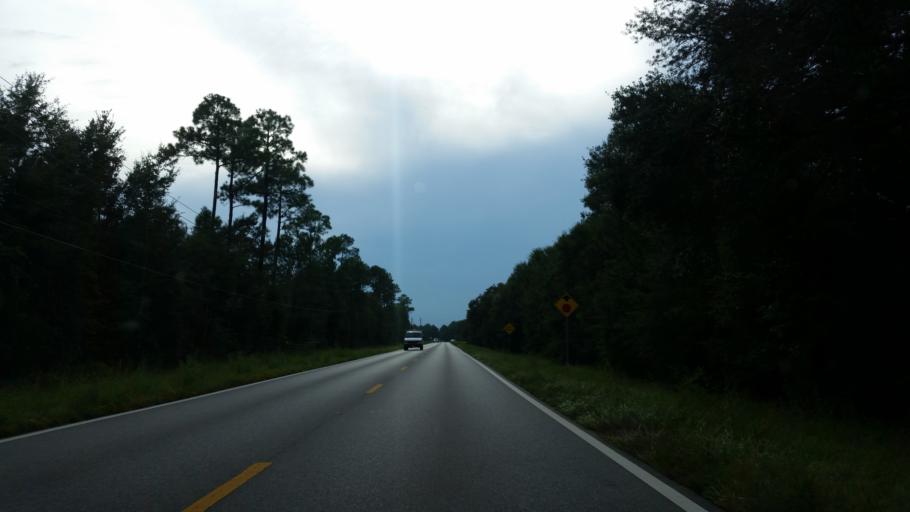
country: US
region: Florida
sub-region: Santa Rosa County
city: Pace
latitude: 30.5742
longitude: -87.1080
